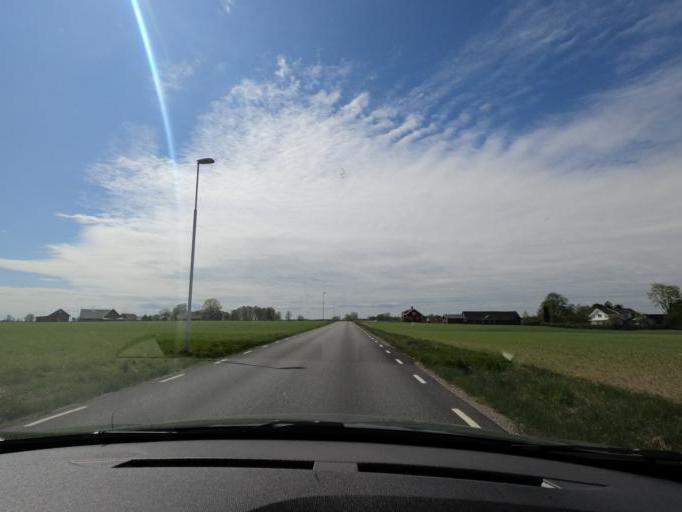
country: SE
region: Joenkoeping
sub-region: Varnamo Kommun
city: Bredaryd
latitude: 57.1329
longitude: 13.7064
